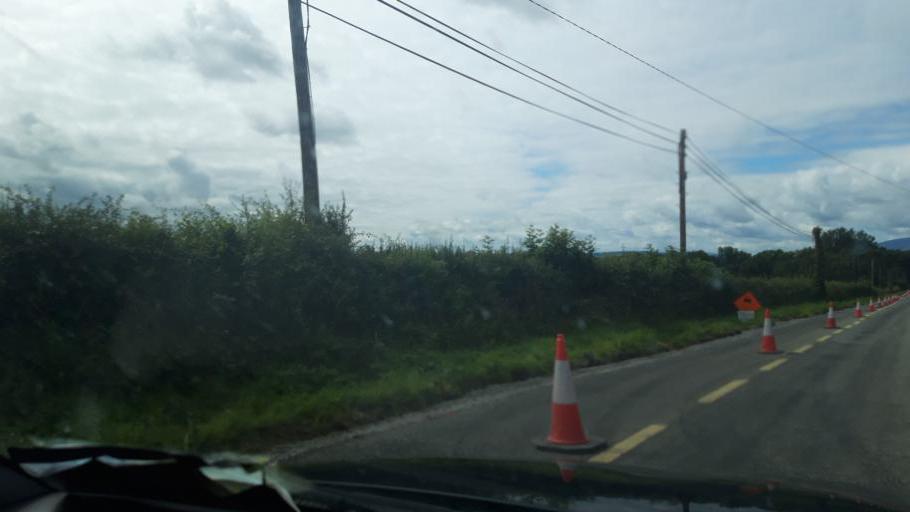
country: IE
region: Leinster
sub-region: Kilkenny
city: Callan
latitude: 52.5615
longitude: -7.3649
